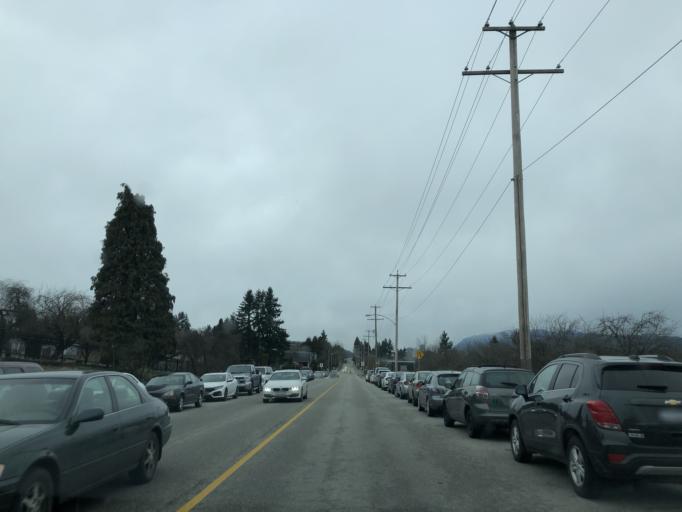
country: CA
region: British Columbia
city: New Westminster
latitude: 49.2213
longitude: -122.8987
